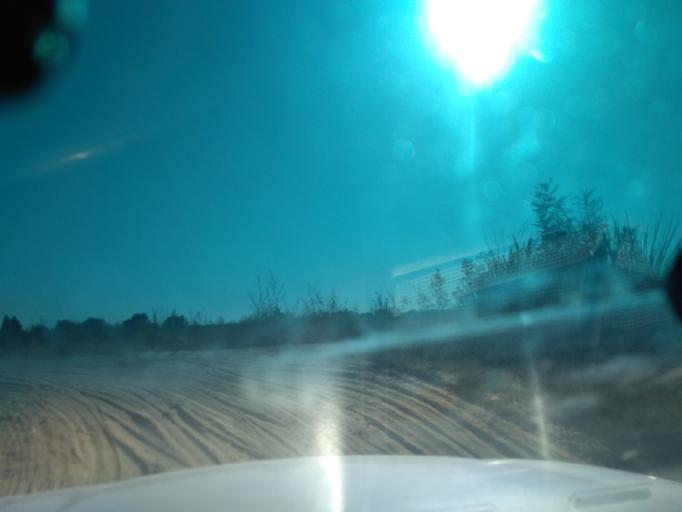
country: TJ
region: Viloyati Sughd
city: Buston
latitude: 40.5553
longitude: 69.0738
